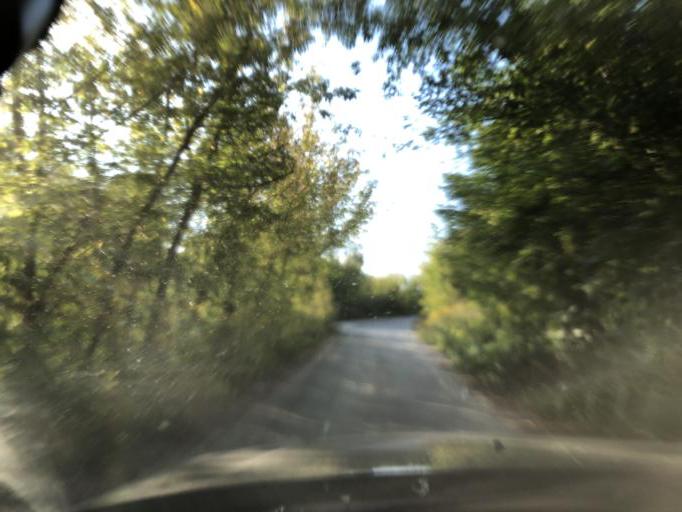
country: RU
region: Tula
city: Mendeleyevskiy
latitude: 54.1840
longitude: 37.5422
